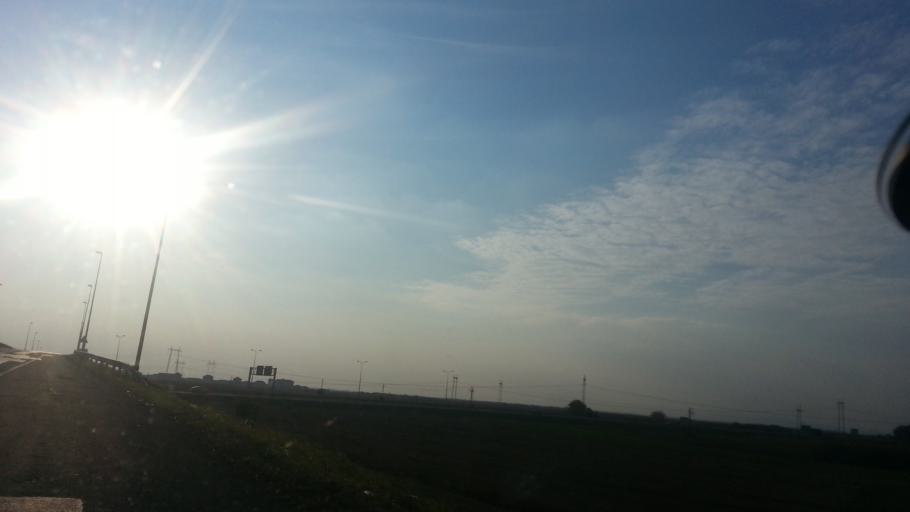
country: RS
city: Novi Karlovci
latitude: 45.0725
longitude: 20.1517
